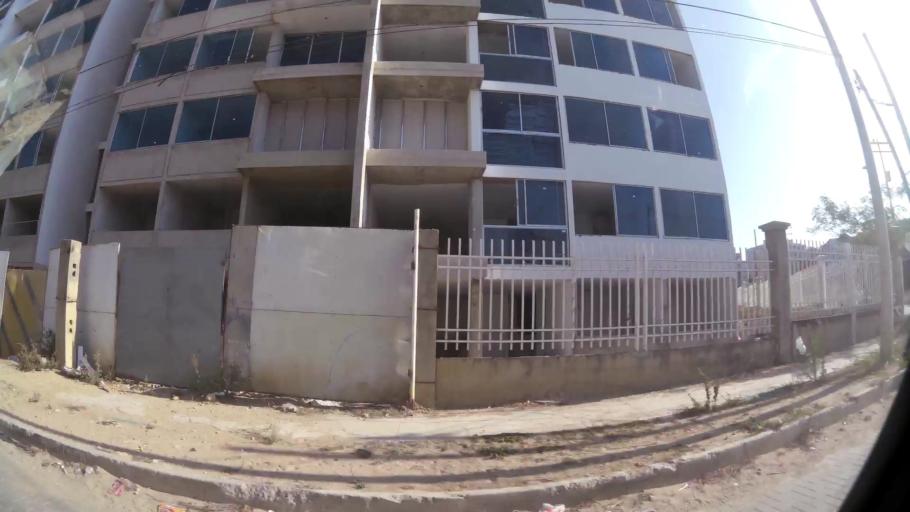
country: CO
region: Atlantico
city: Barranquilla
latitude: 11.0068
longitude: -74.8376
